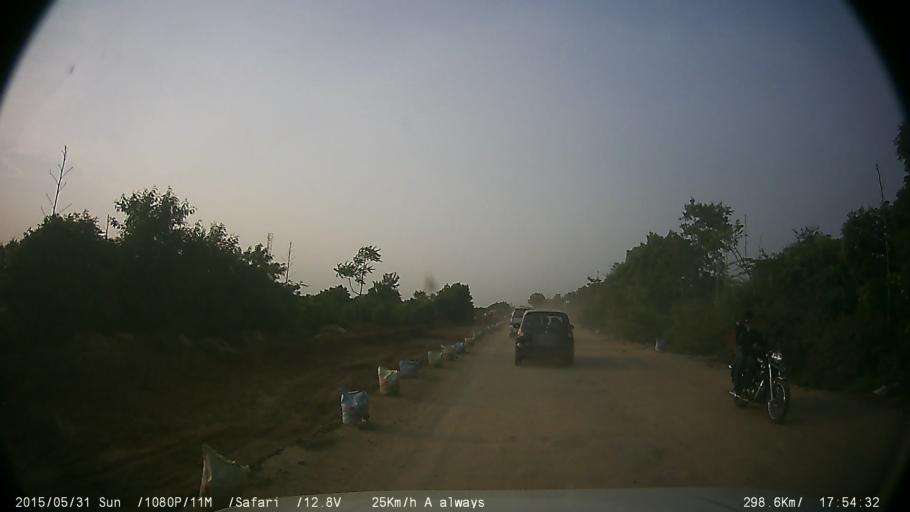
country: IN
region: Karnataka
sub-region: Mysore
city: Nanjangud
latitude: 11.9876
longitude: 76.6696
